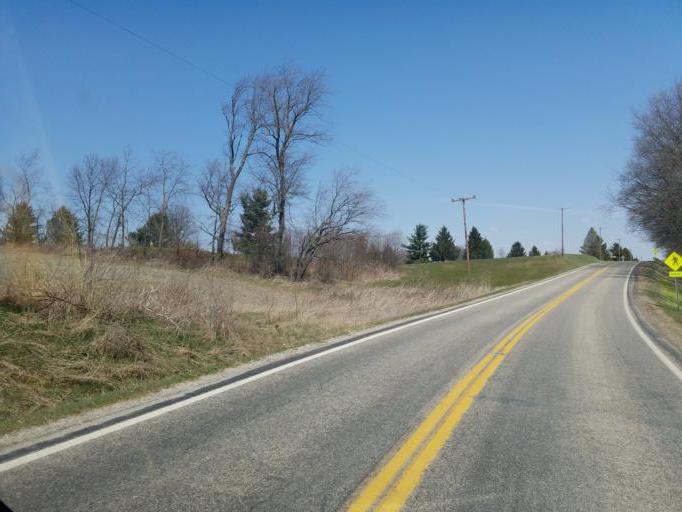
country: US
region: Ohio
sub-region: Ashland County
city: Loudonville
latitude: 40.6711
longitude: -82.1483
